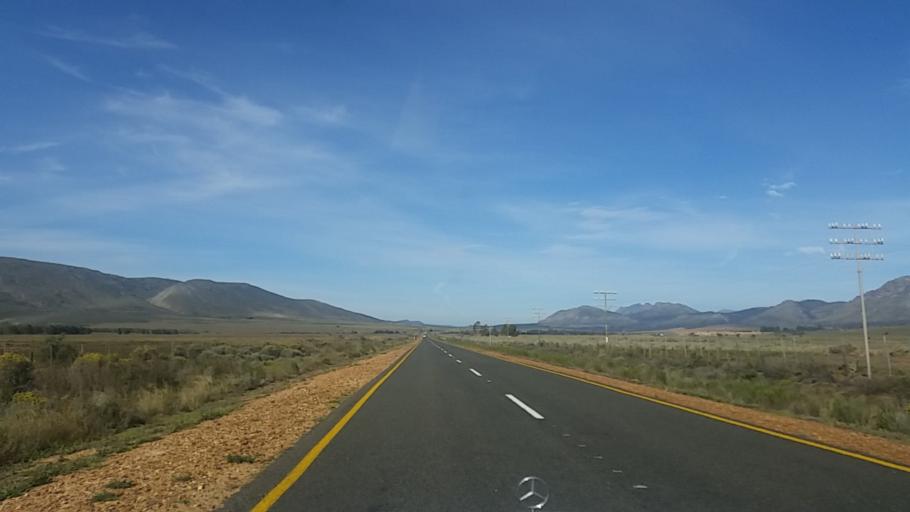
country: ZA
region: Western Cape
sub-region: Eden District Municipality
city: George
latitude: -33.8104
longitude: 22.5417
